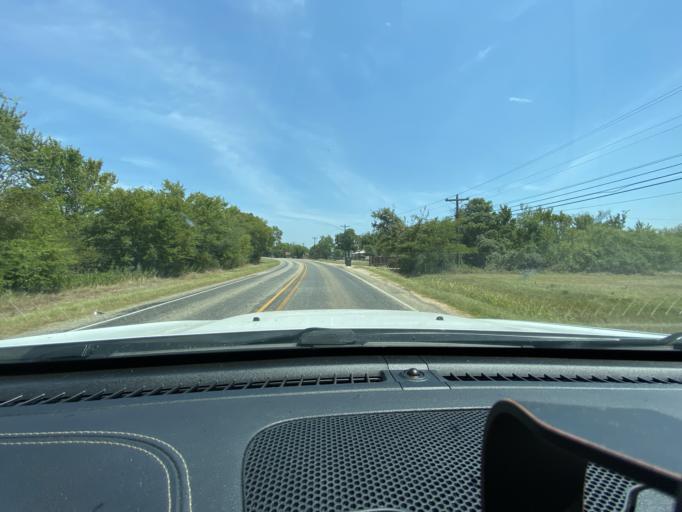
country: US
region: Texas
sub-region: Lee County
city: Giddings
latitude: 30.1730
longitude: -96.9394
